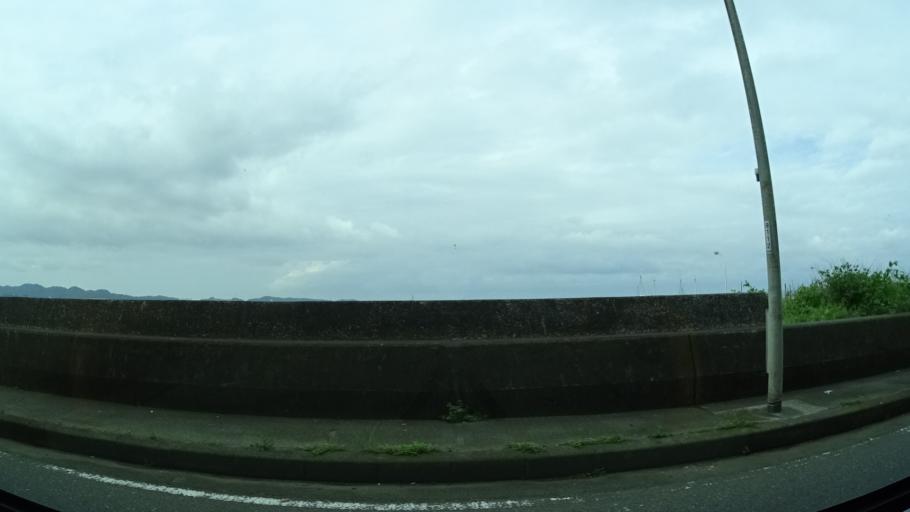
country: JP
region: Kanagawa
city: Miura
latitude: 35.1593
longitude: 139.6632
